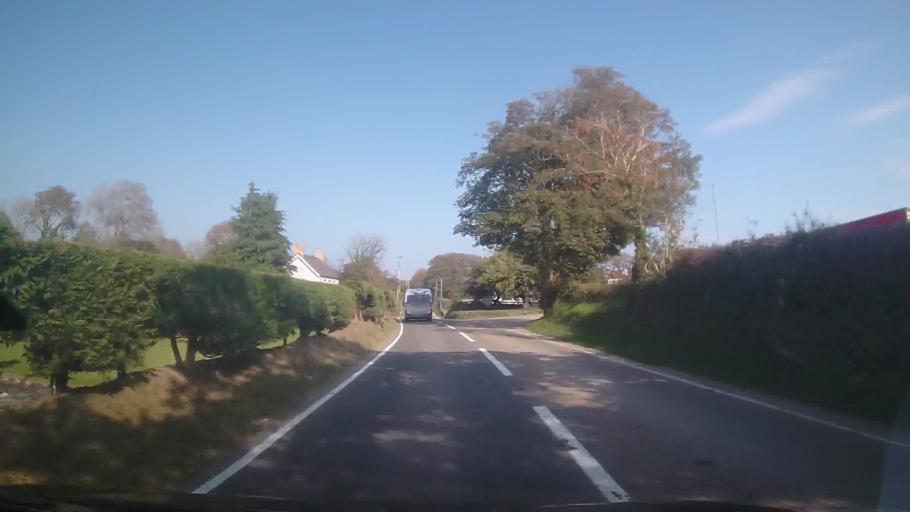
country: GB
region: Wales
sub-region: Pembrokeshire
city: Crymych
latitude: 52.0090
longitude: -4.7198
